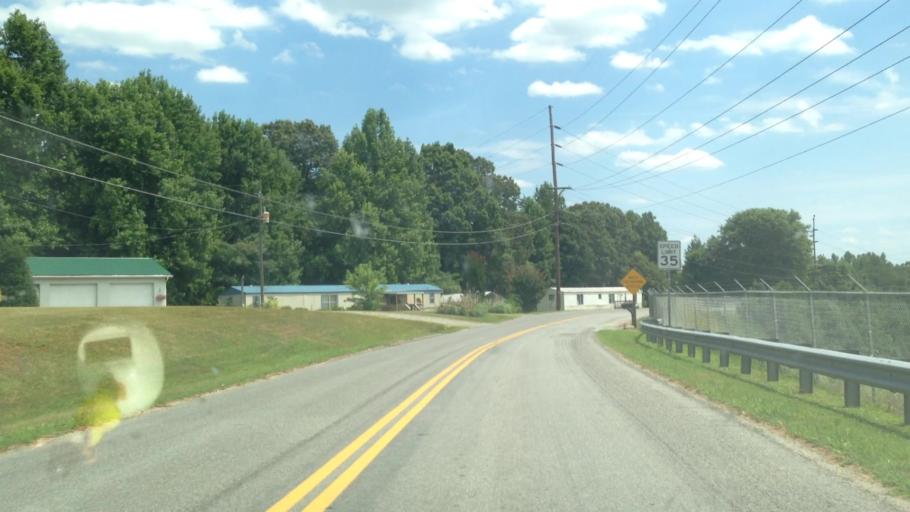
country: US
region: Virginia
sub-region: Henry County
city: Chatmoss
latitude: 36.6230
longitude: -79.8515
